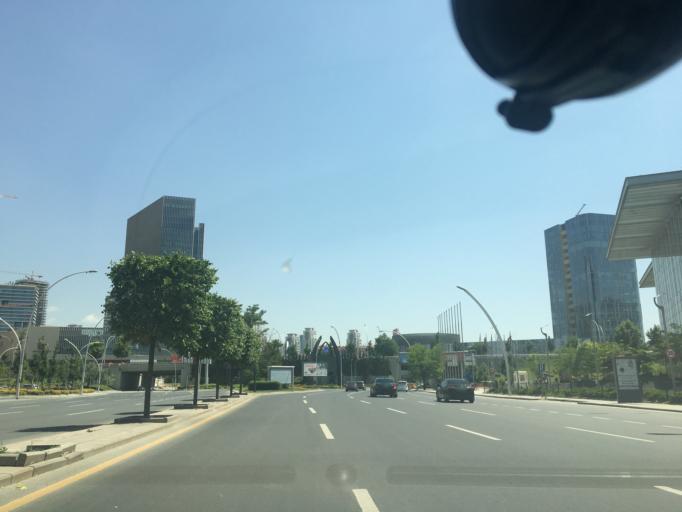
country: TR
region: Ankara
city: Ankara
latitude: 39.9121
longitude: 32.8035
